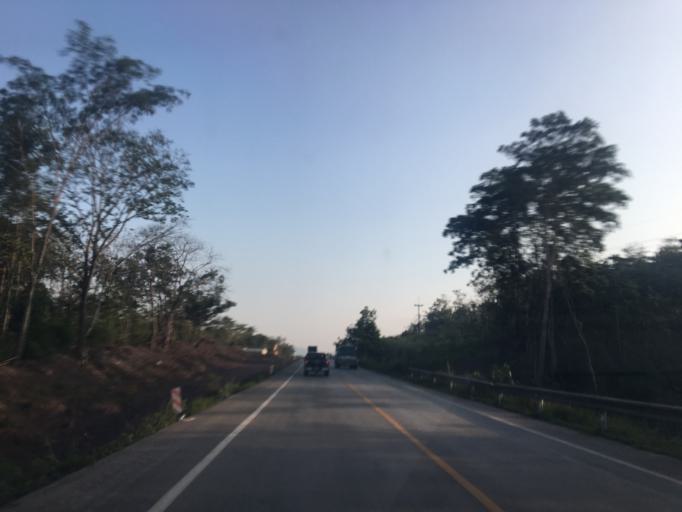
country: TH
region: Lampang
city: Ngao
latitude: 18.6872
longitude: 100.0041
